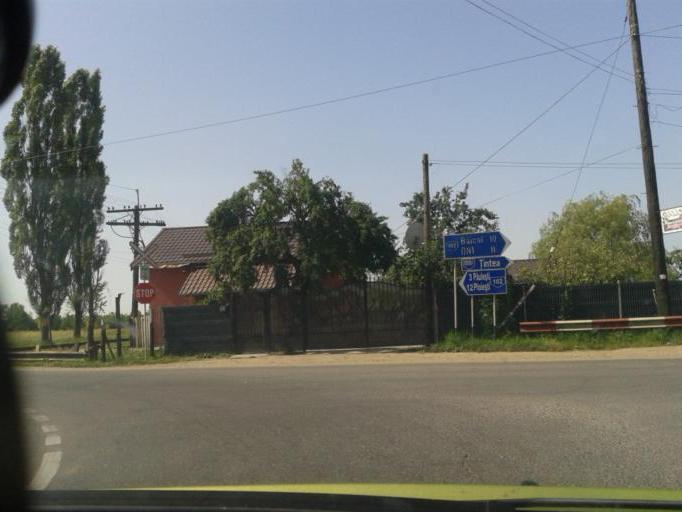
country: RO
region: Prahova
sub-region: Comuna Paulesti
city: Gageni
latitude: 45.0343
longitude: 25.9401
